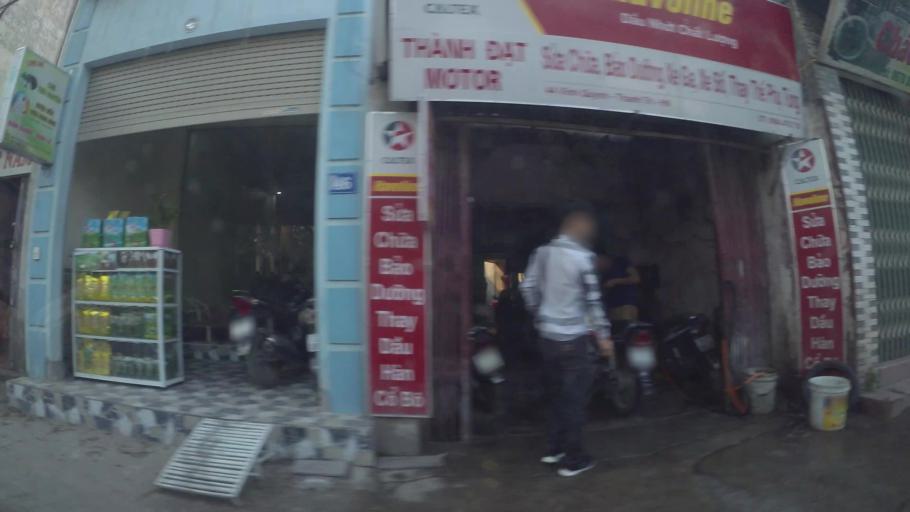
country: VN
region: Ha Noi
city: Van Dien
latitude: 20.9424
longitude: 105.8416
